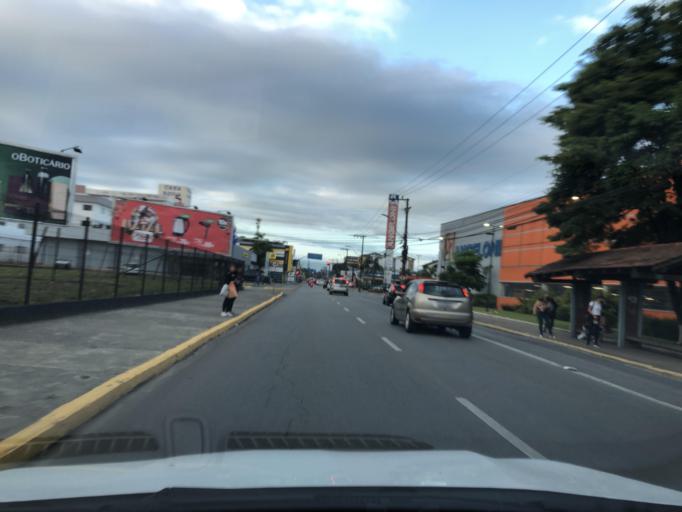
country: BR
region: Santa Catarina
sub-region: Joinville
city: Joinville
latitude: -26.2790
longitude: -48.8497
